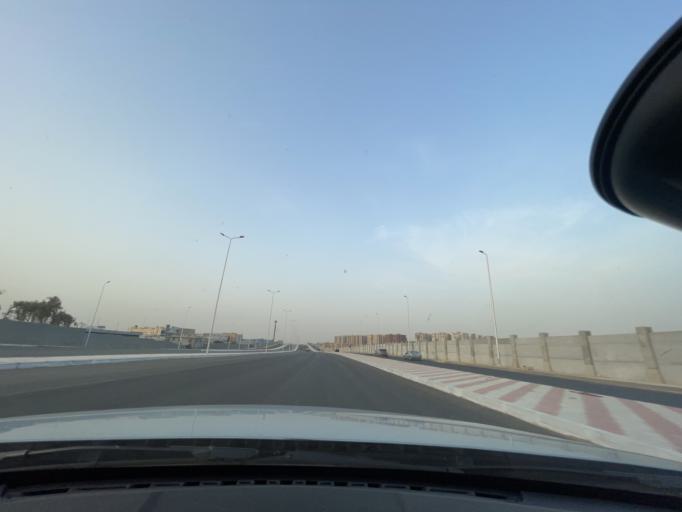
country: EG
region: Muhafazat al Qahirah
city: Cairo
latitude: 30.0287
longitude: 31.3481
